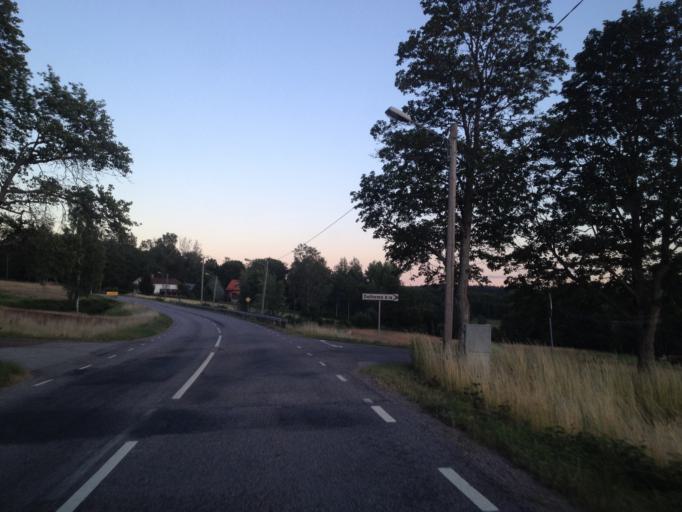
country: SE
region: Kalmar
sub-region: Vasterviks Kommun
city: Overum
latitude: 57.9881
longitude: 16.1876
